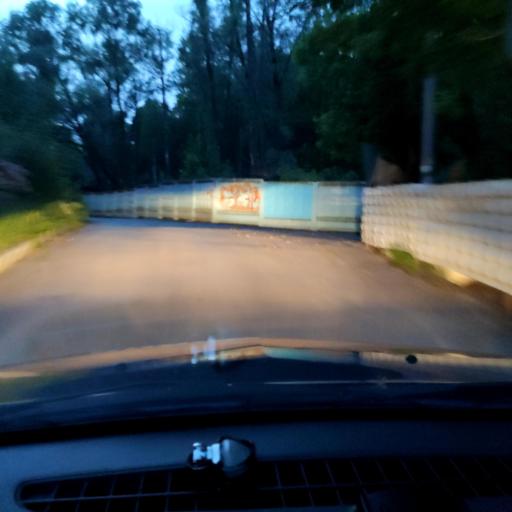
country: RU
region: Voronezj
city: Ramon'
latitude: 51.8274
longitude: 39.2800
